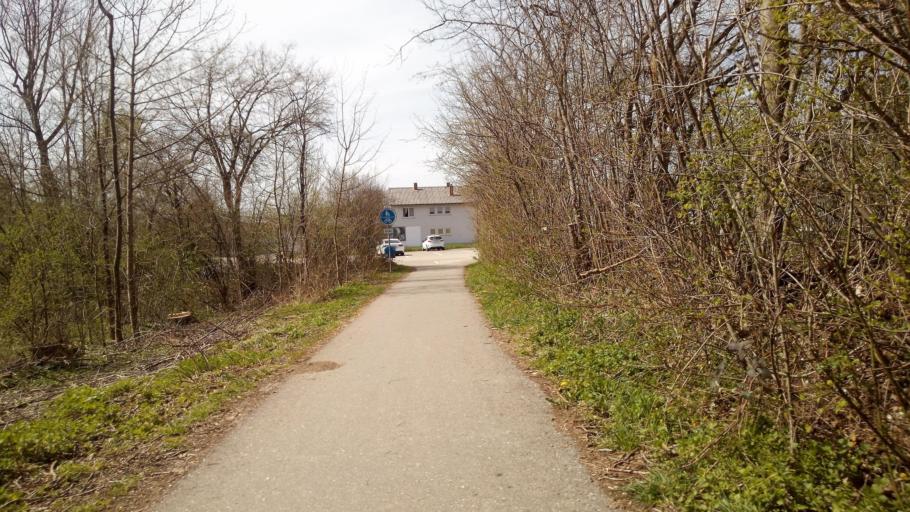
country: DE
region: Baden-Wuerttemberg
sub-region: Regierungsbezirk Stuttgart
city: Donzdorf
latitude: 48.6877
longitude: 9.8018
